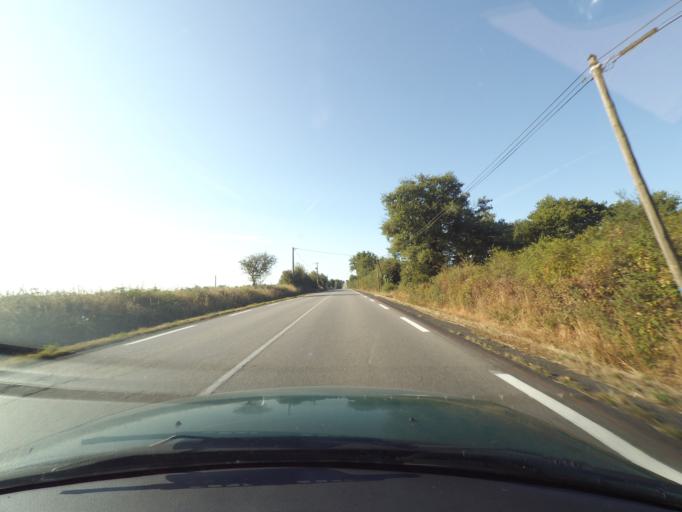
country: FR
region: Poitou-Charentes
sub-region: Departement des Deux-Sevres
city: Chiche
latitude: 46.7646
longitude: -0.3131
